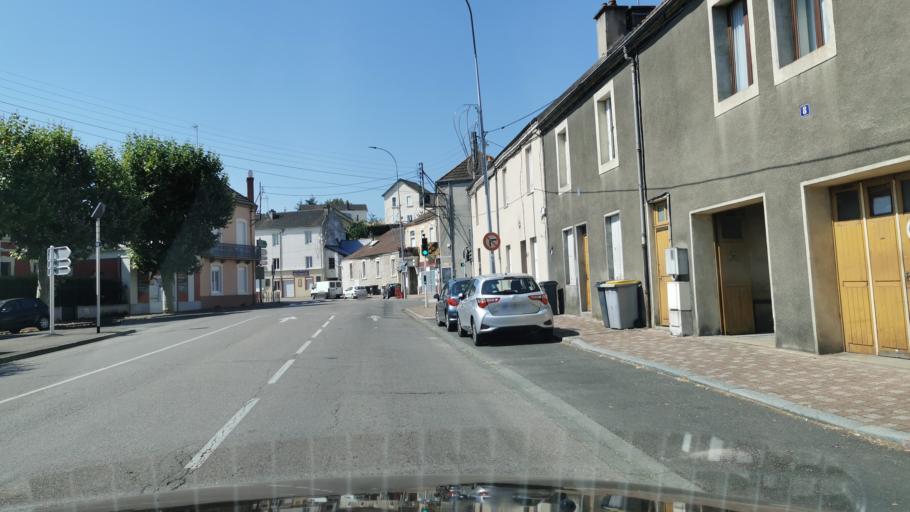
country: FR
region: Bourgogne
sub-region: Departement de Saone-et-Loire
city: Le Creusot
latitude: 46.8045
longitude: 4.4134
